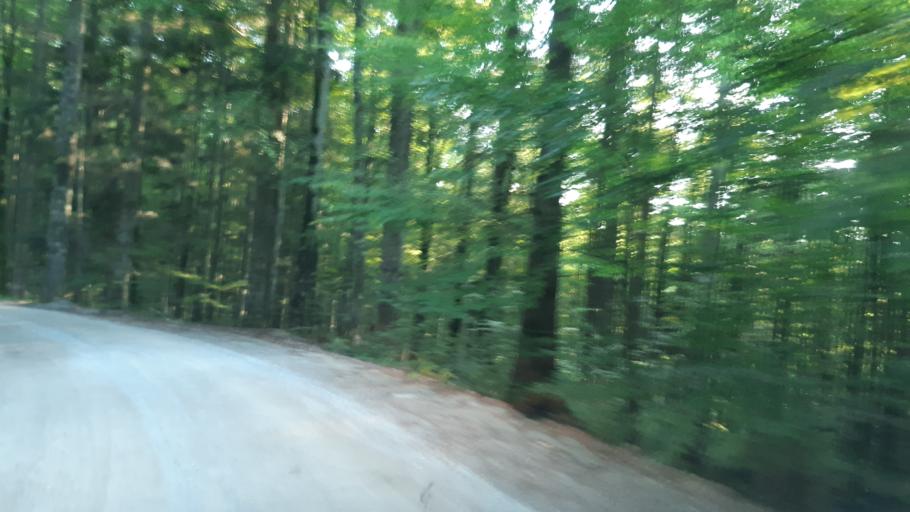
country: SI
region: Kocevje
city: Kocevje
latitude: 45.6731
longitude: 14.9718
